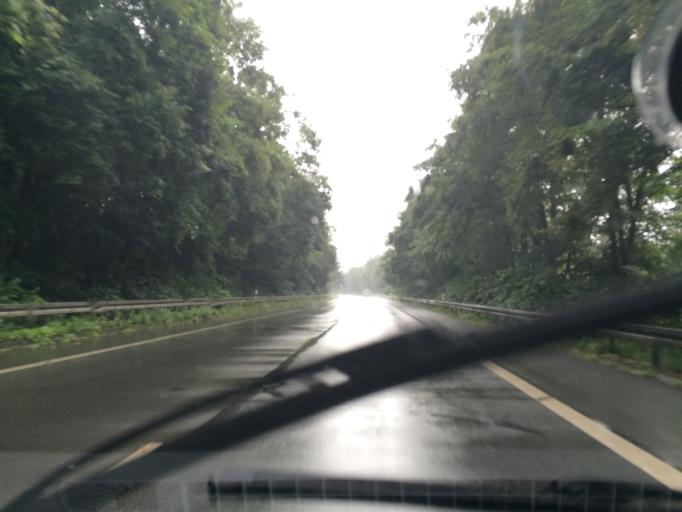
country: DE
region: North Rhine-Westphalia
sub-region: Regierungsbezirk Munster
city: Haltern
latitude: 51.7715
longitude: 7.2348
